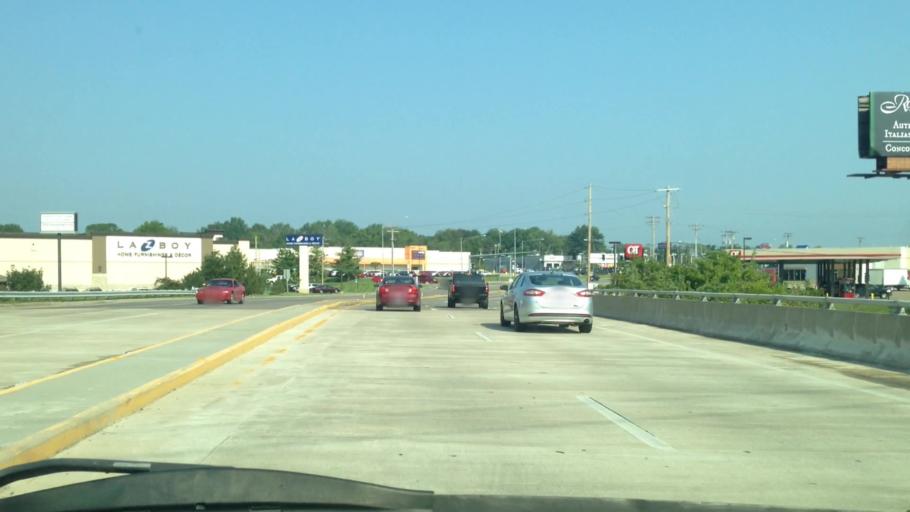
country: US
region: Missouri
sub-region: Saint Louis County
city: Green Park
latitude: 38.5136
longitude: -90.3407
